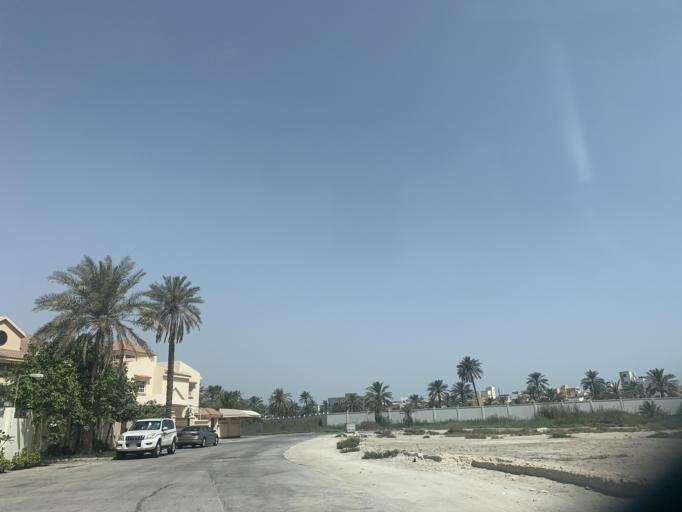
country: BH
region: Manama
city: Jidd Hafs
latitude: 26.1997
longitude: 50.5552
